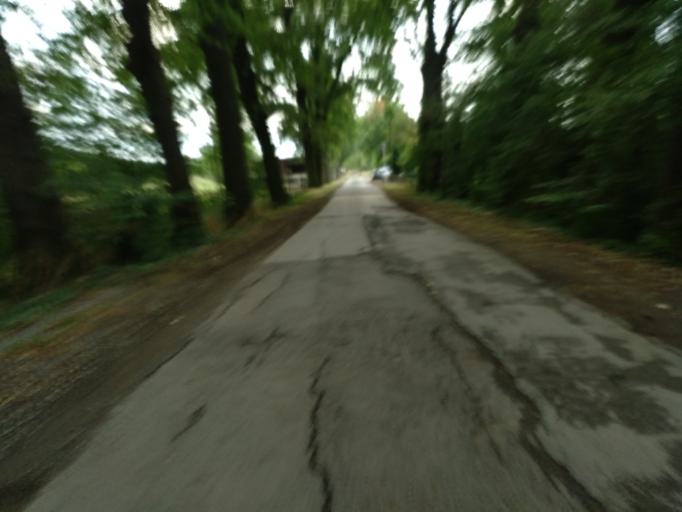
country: DE
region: North Rhine-Westphalia
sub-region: Regierungsbezirk Dusseldorf
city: Krefeld
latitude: 51.4030
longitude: 6.5449
